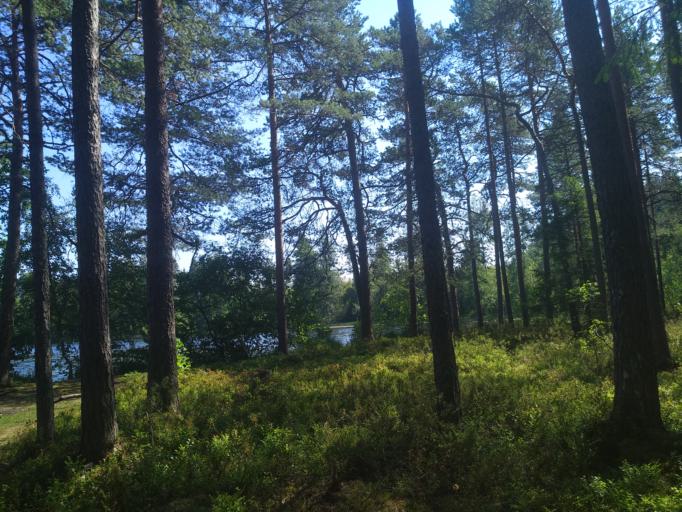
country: EE
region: Harju
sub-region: Kuusalu vald
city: Kuusalu
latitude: 59.2948
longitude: 25.6712
